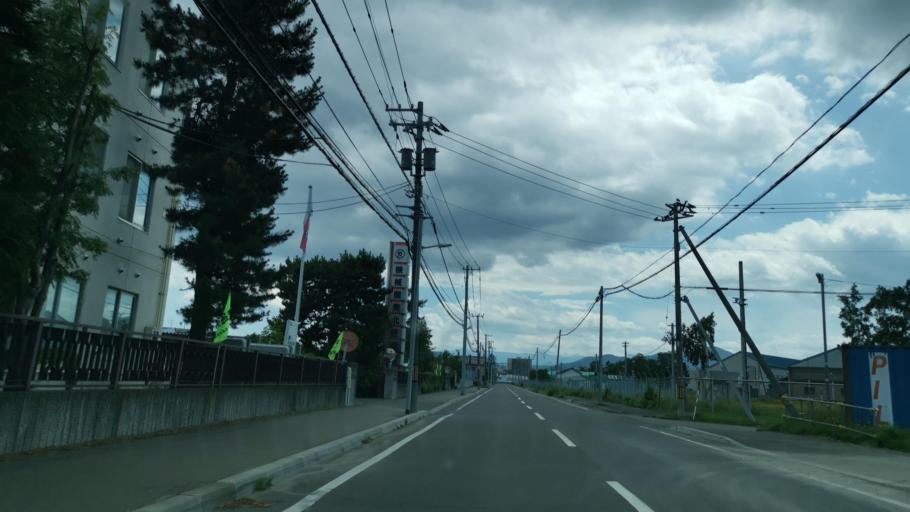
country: JP
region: Hokkaido
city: Sapporo
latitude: 43.0733
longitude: 141.3918
